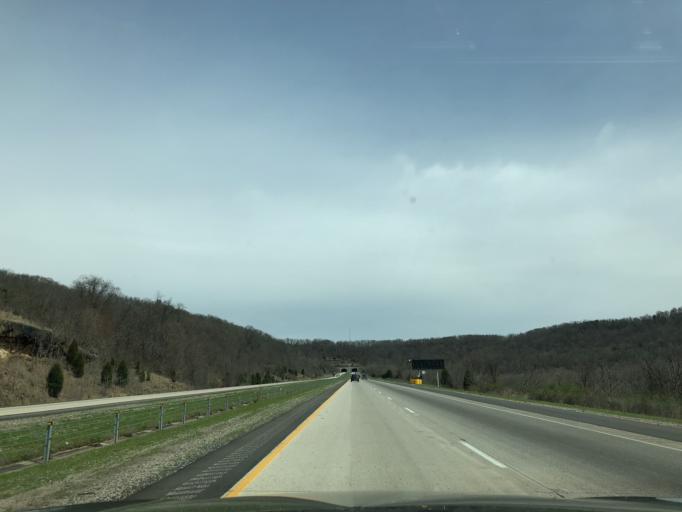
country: US
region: Arkansas
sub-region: Washington County
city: West Fork
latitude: 35.7555
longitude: -94.1969
